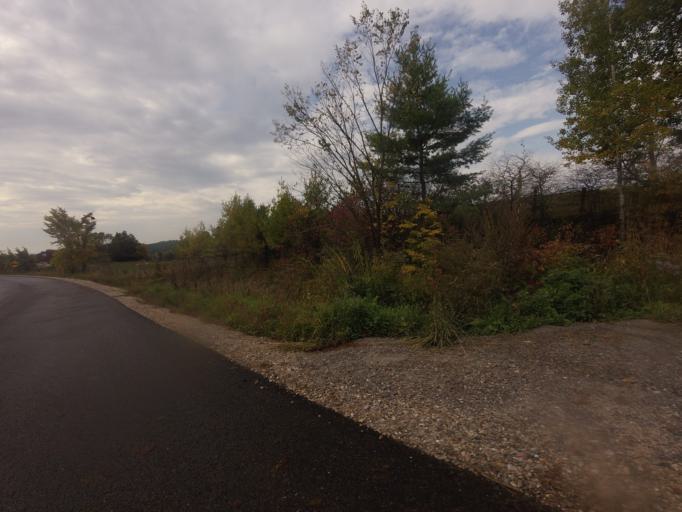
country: CA
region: Quebec
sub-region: Outaouais
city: Wakefield
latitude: 45.9821
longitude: -75.9371
